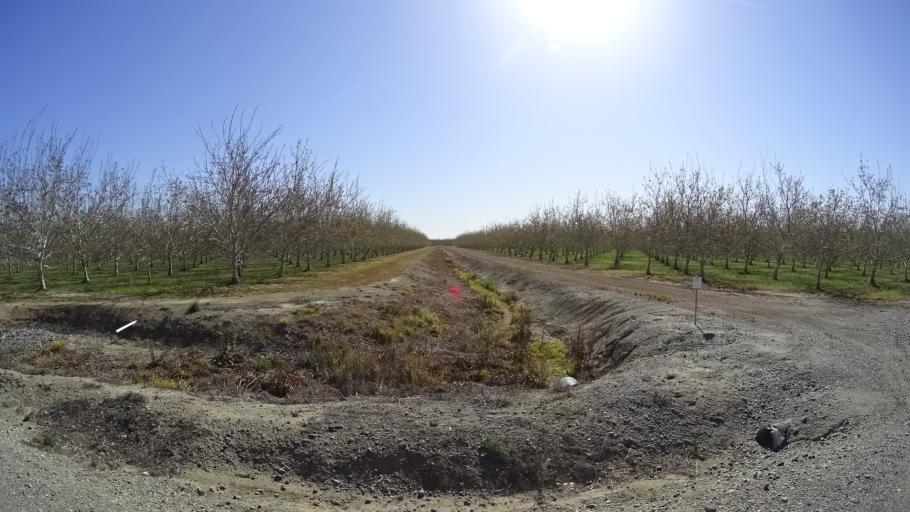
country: US
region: California
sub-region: Glenn County
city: Hamilton City
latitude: 39.6931
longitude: -122.0742
